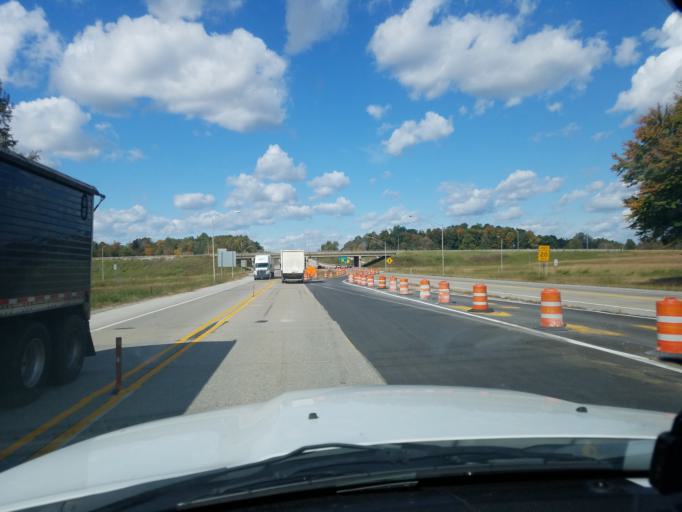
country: US
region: Kentucky
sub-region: Ohio County
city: Hartford
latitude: 37.4560
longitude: -86.8807
